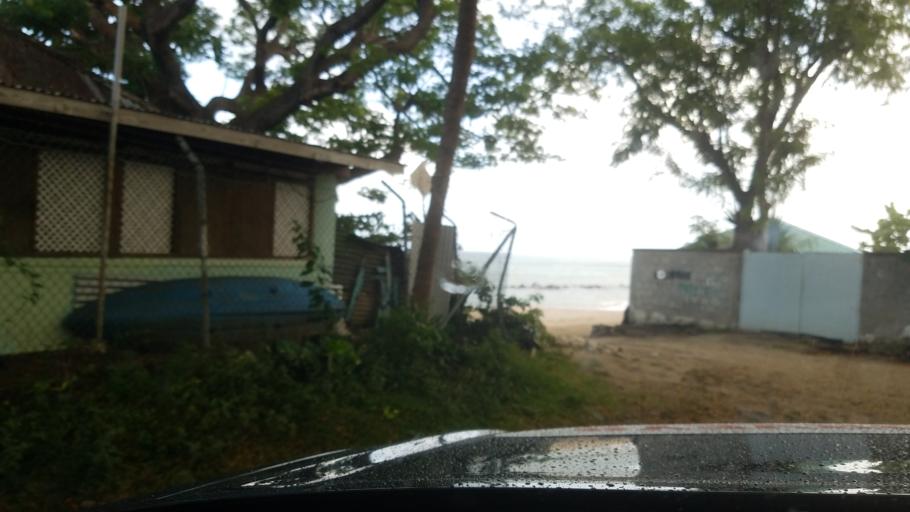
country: LC
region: Castries Quarter
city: Bisee
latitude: 14.0235
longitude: -60.9854
